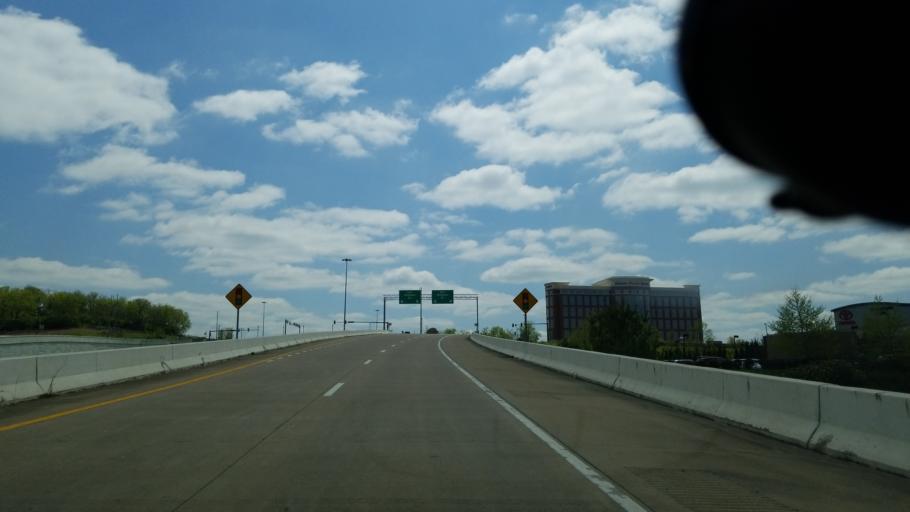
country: US
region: Tennessee
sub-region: Williamson County
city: Franklin
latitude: 35.9366
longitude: -86.8185
